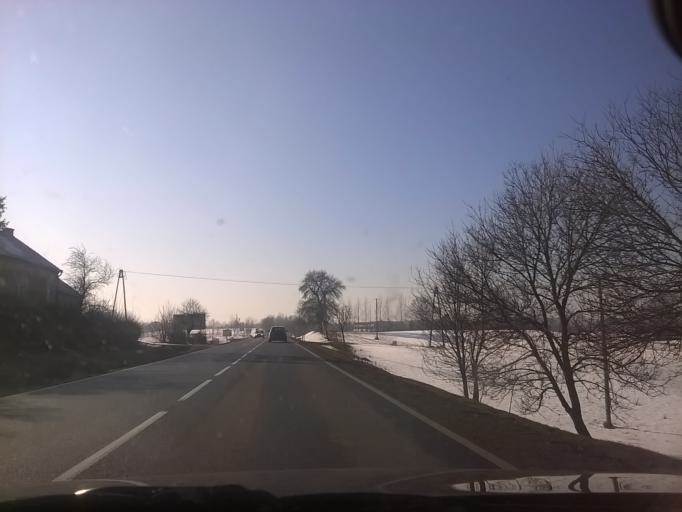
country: PL
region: Warmian-Masurian Voivodeship
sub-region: Powiat mragowski
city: Mragowo
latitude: 53.8422
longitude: 21.2171
